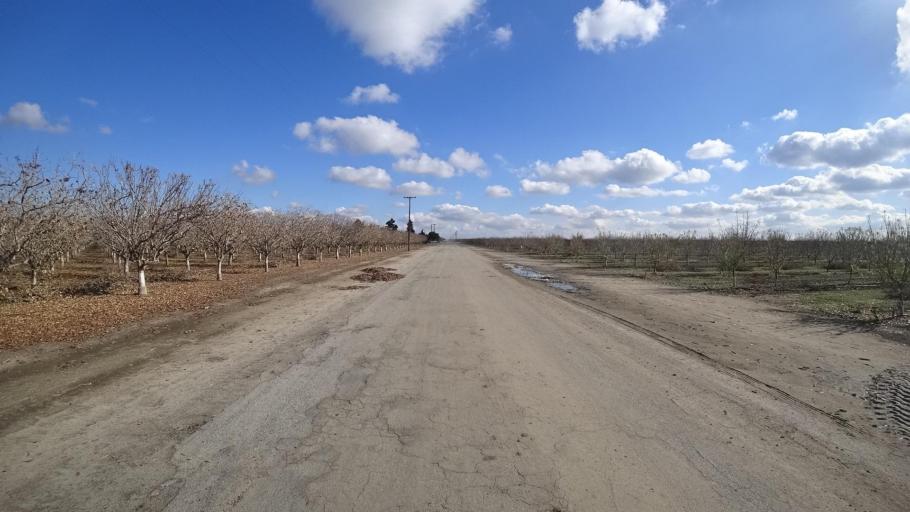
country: US
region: California
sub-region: Kern County
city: Wasco
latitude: 35.6669
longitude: -119.3245
